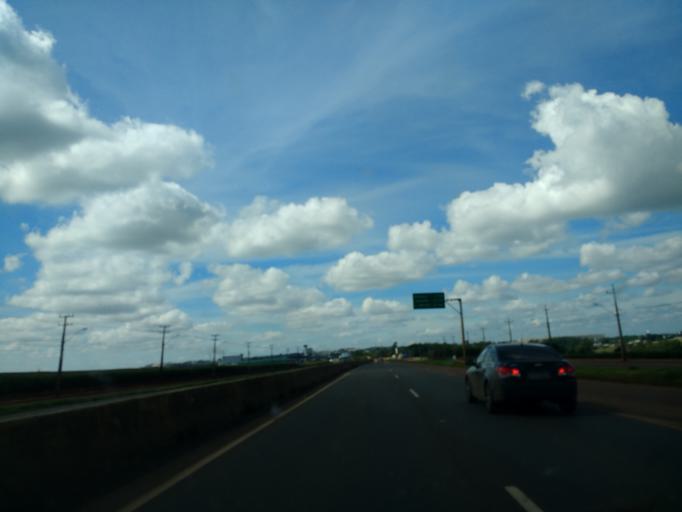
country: BR
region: Parana
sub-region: Paicandu
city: Paicandu
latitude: -23.4565
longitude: -52.0197
